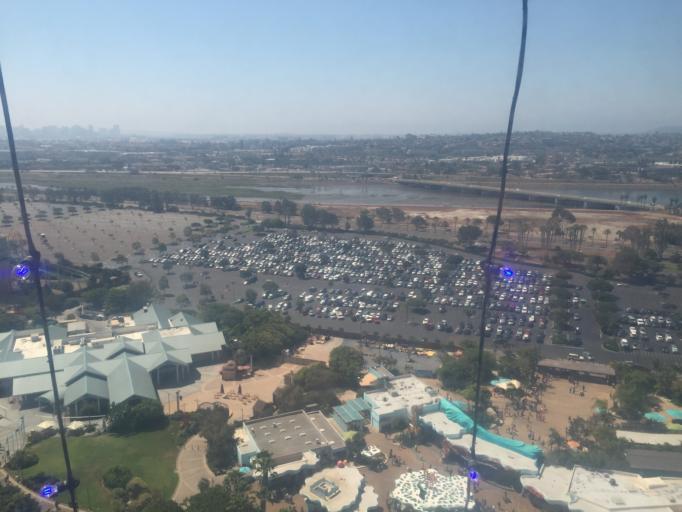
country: US
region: California
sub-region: San Diego County
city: San Diego
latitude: 32.7654
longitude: -117.2267
